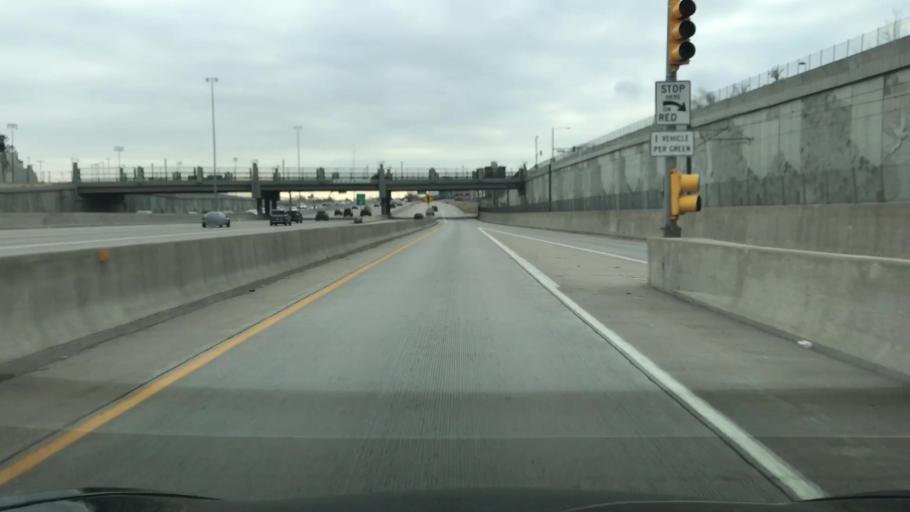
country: US
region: Colorado
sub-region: Arapahoe County
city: Glendale
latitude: 39.6881
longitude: -104.9705
